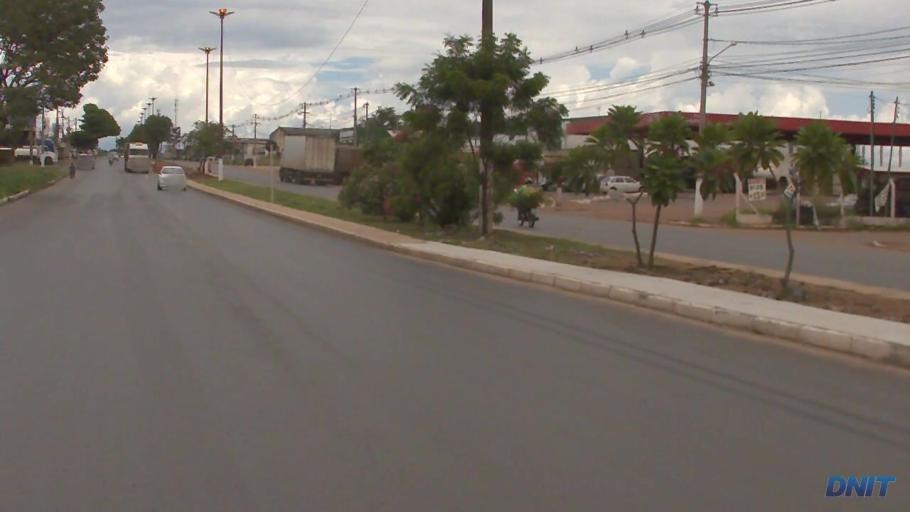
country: BR
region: Mato Grosso
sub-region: Varzea Grande
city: Varzea Grande
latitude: -15.6430
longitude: -56.1798
